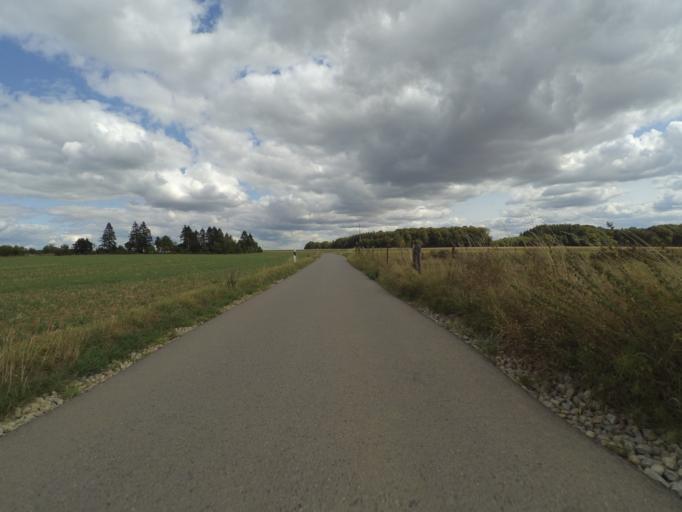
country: LU
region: Grevenmacher
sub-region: Canton de Remich
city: Dalheim
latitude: 49.5389
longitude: 6.2652
